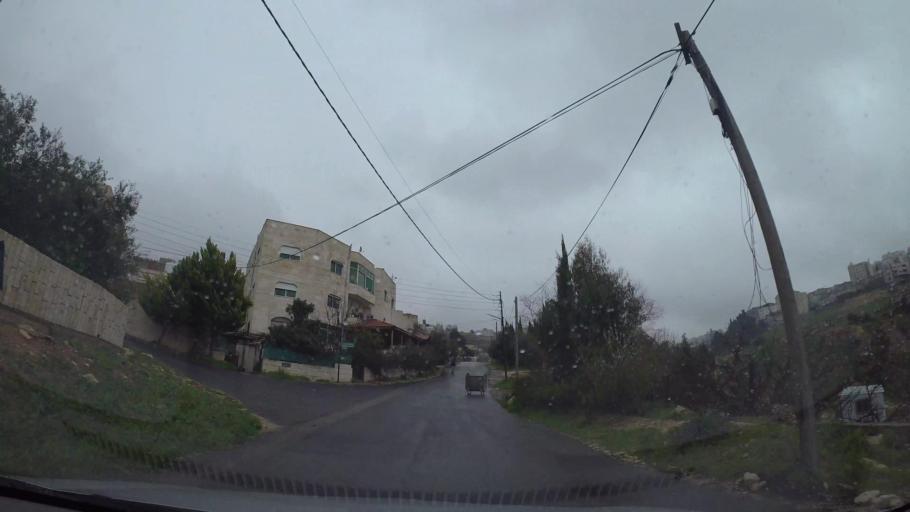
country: JO
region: Amman
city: Al Jubayhah
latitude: 32.0320
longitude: 35.8402
